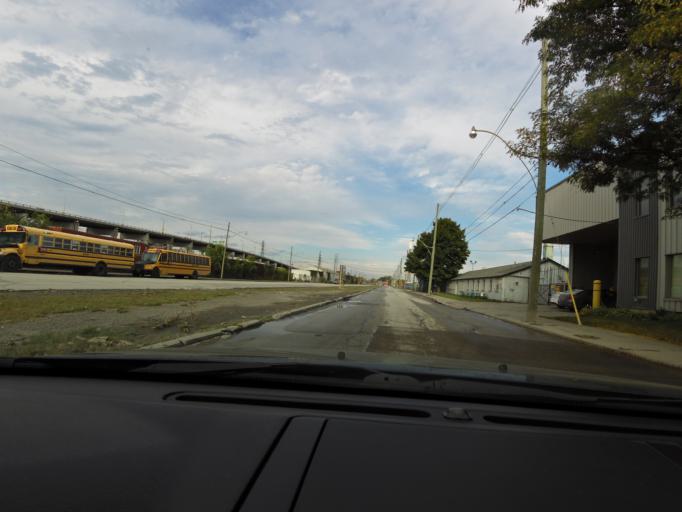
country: CA
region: Ontario
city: Toronto
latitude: 43.6480
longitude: -79.3510
